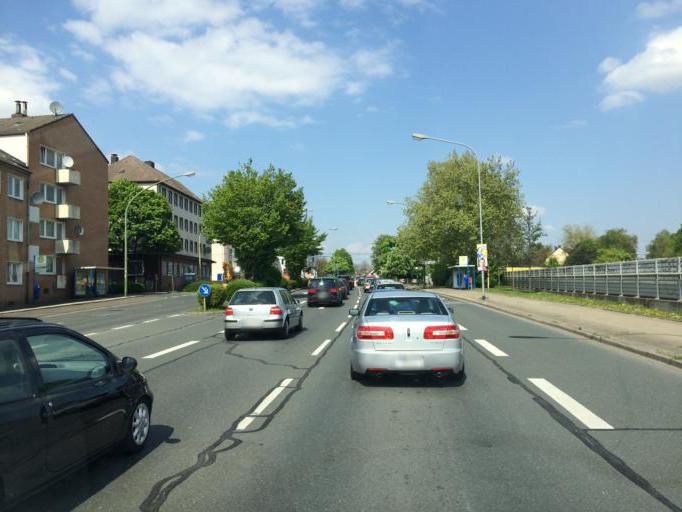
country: DE
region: North Rhine-Westphalia
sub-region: Regierungsbezirk Dusseldorf
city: Essen
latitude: 51.4474
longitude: 7.0373
